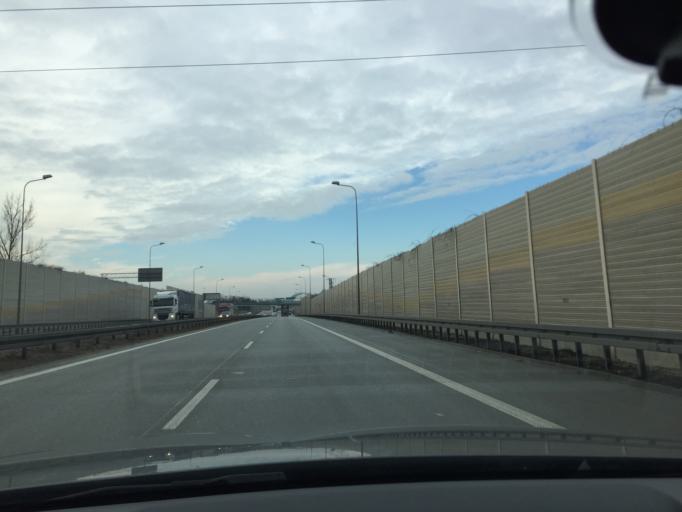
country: PL
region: Lodz Voivodeship
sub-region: Powiat skierniewicki
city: Kowiesy
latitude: 51.9227
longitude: 20.4593
